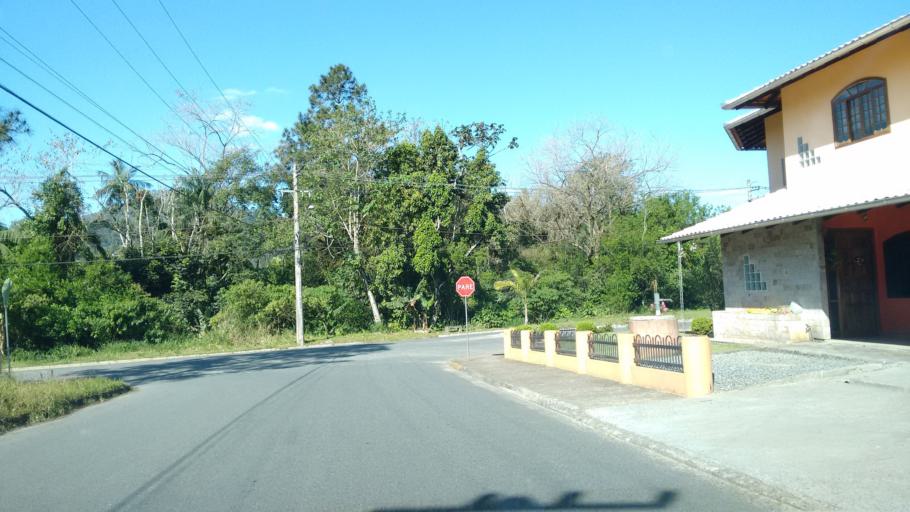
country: BR
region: Santa Catarina
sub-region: Pomerode
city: Pomerode
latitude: -26.7558
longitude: -49.1749
